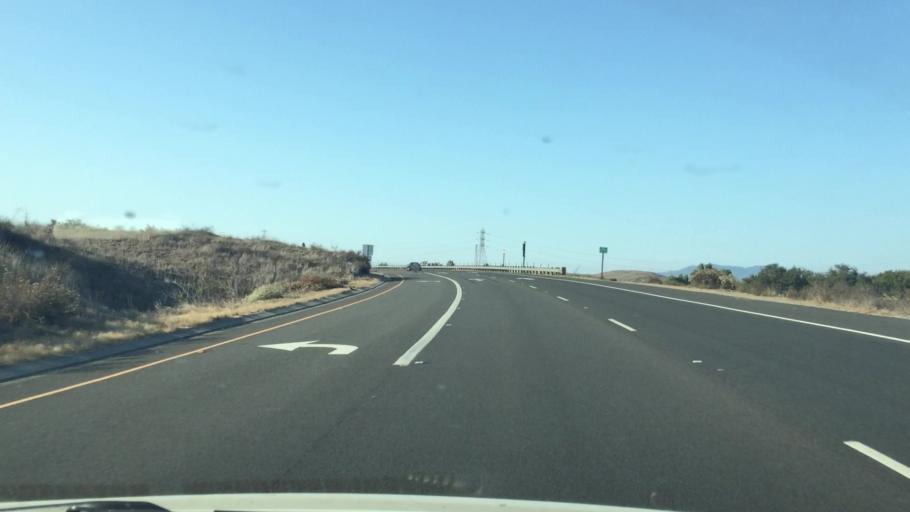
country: US
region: California
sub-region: Orange County
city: Laguna Woods
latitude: 33.6052
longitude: -117.7608
